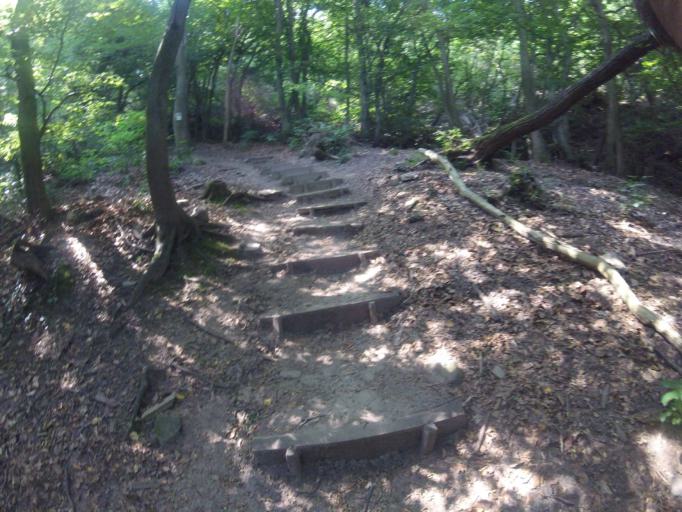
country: HU
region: Veszprem
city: Badacsonytomaj
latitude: 46.8073
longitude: 17.4958
